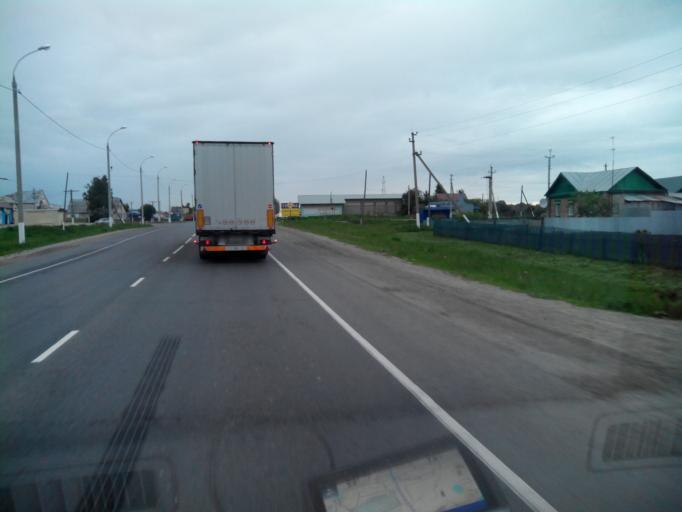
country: RU
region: Penza
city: Chemodanovka
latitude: 53.2171
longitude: 45.2911
